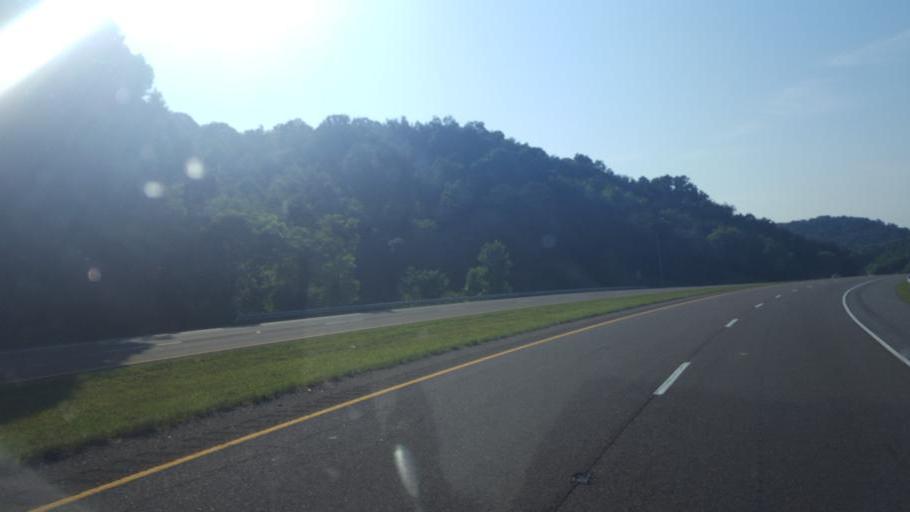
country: US
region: Tennessee
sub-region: Carter County
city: Elizabethton
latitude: 36.3795
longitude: -82.2199
